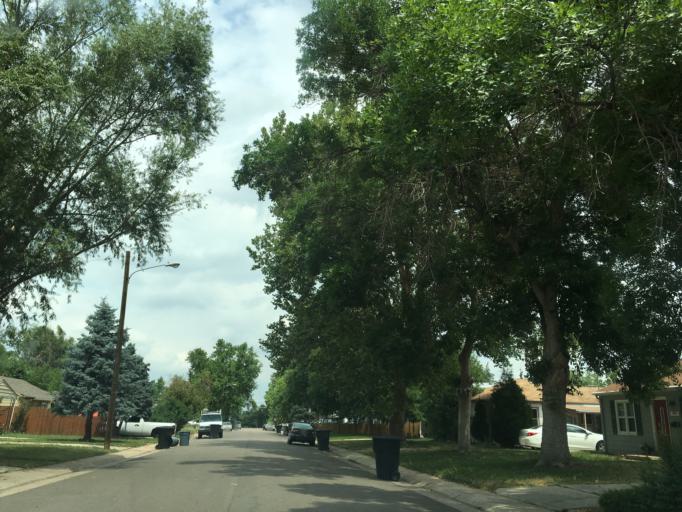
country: US
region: Colorado
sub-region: Arapahoe County
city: Sheridan
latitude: 39.6804
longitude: -105.0321
